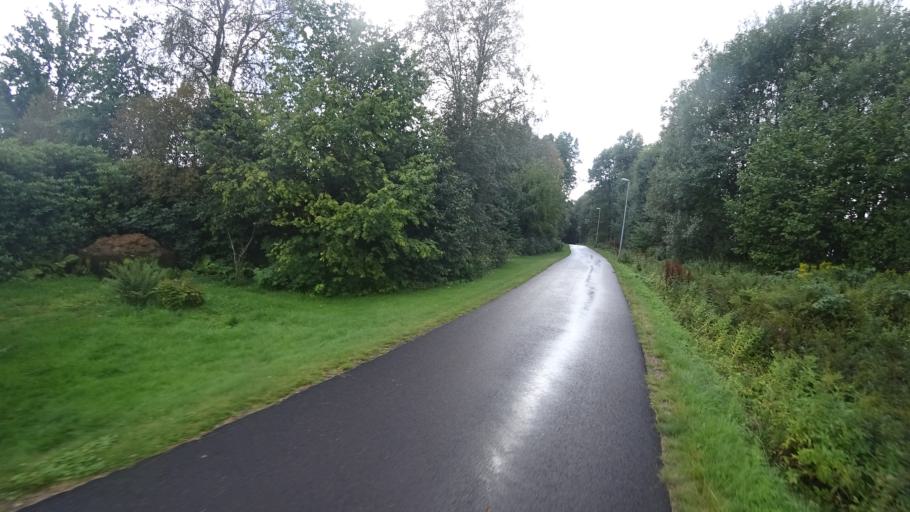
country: SE
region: Vaestra Goetaland
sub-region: Partille Kommun
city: Ojersjo
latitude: 57.6973
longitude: 12.1318
